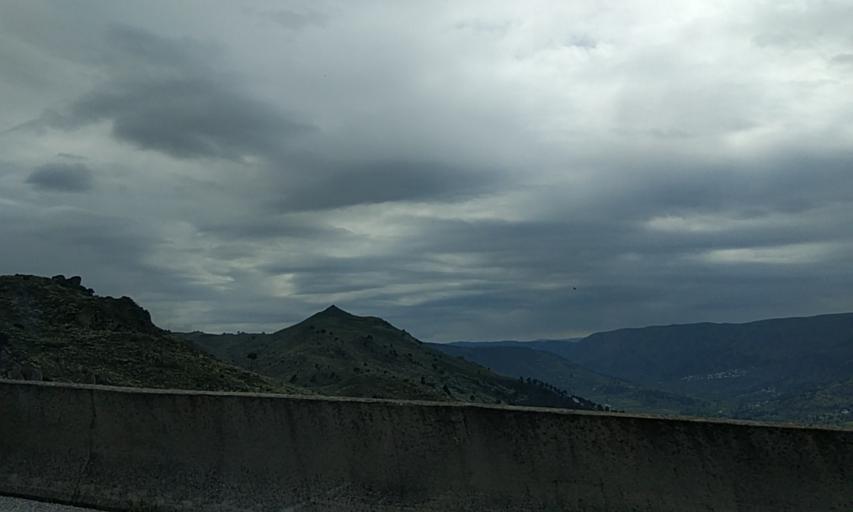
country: PT
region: Guarda
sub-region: Guarda
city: Guarda
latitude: 40.5951
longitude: -7.2755
